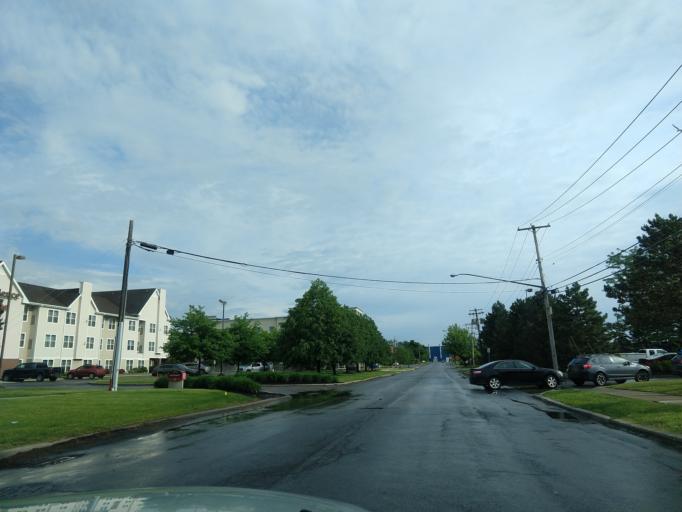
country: US
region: New York
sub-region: Erie County
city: Cheektowaga
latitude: 42.9080
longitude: -78.7715
